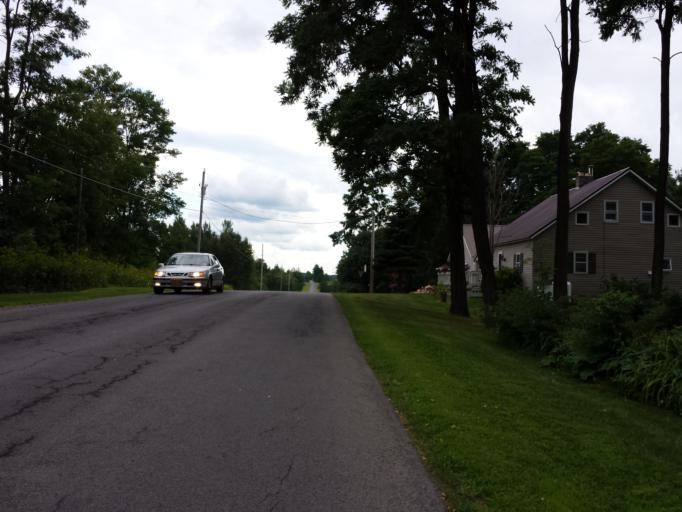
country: US
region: New York
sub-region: St. Lawrence County
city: Potsdam
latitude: 44.7075
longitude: -75.0002
